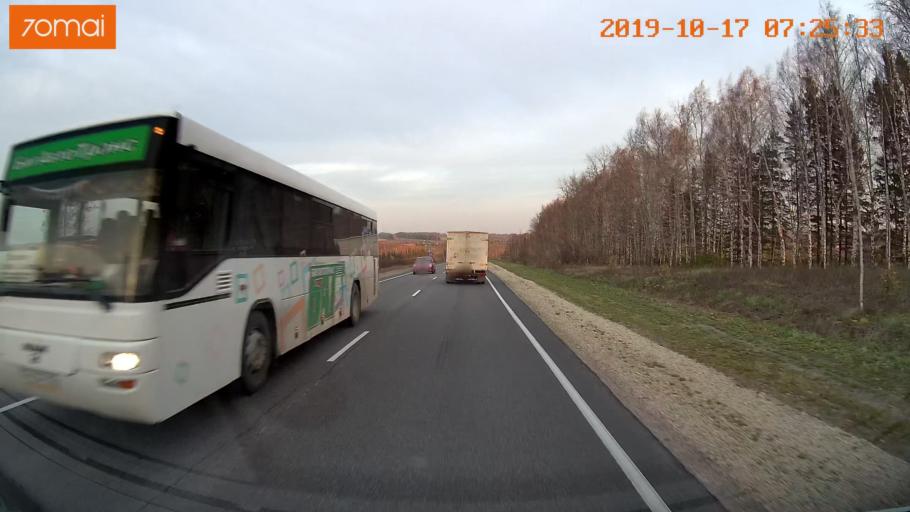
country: RU
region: Ivanovo
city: Gavrilov Posad
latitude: 56.3503
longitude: 40.1024
